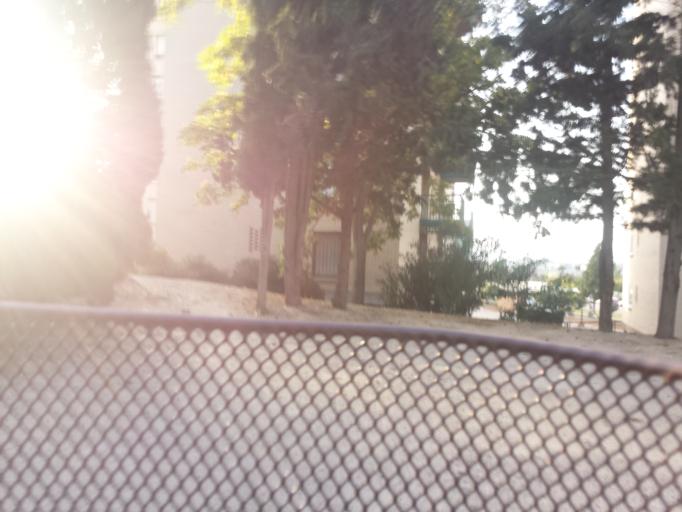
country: ES
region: Aragon
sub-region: Provincia de Zaragoza
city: Delicias
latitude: 41.6566
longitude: -0.9141
